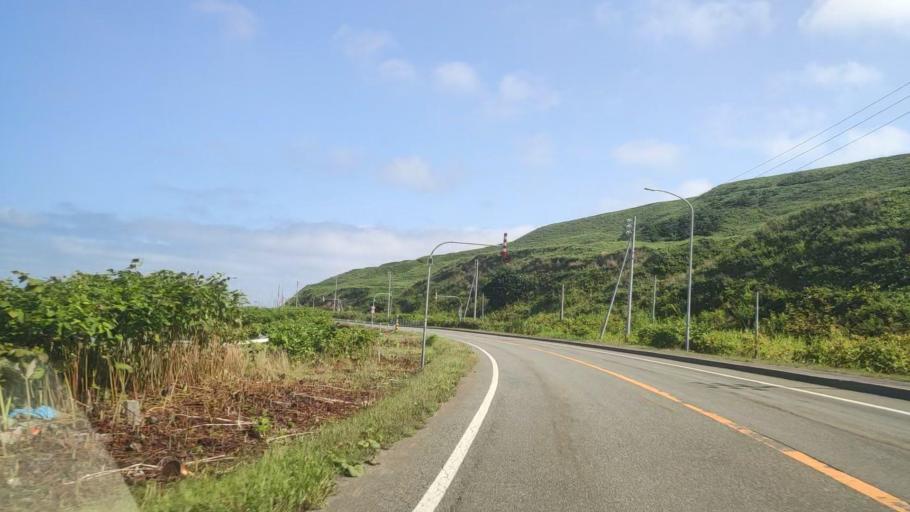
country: JP
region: Hokkaido
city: Makubetsu
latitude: 45.5023
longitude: 141.8927
